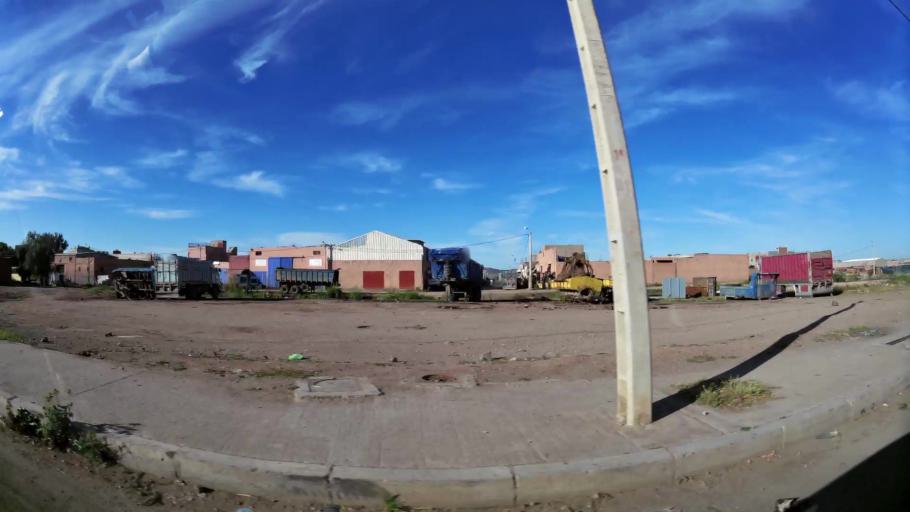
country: MA
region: Marrakech-Tensift-Al Haouz
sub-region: Marrakech
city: Marrakesh
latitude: 31.6840
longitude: -8.0607
